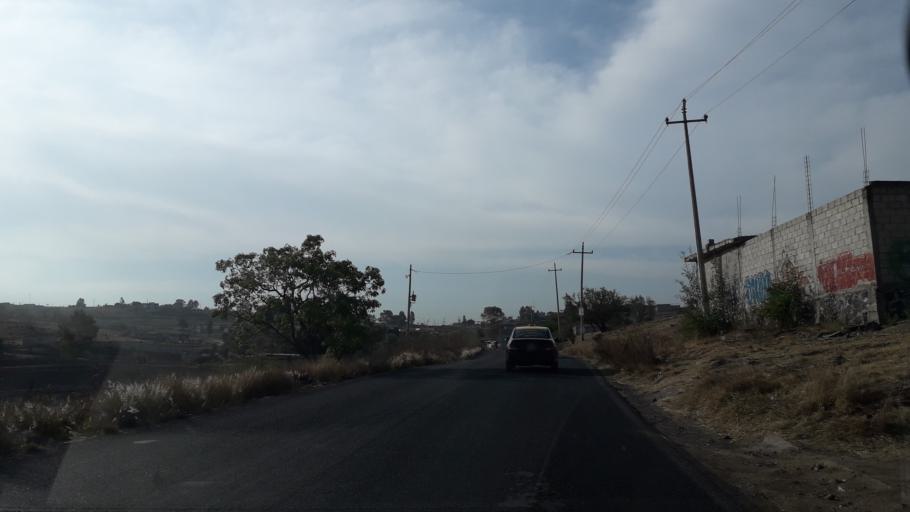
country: MX
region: Puebla
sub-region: Puebla
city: San Andres Azumiatla
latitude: 18.9163
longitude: -98.2459
